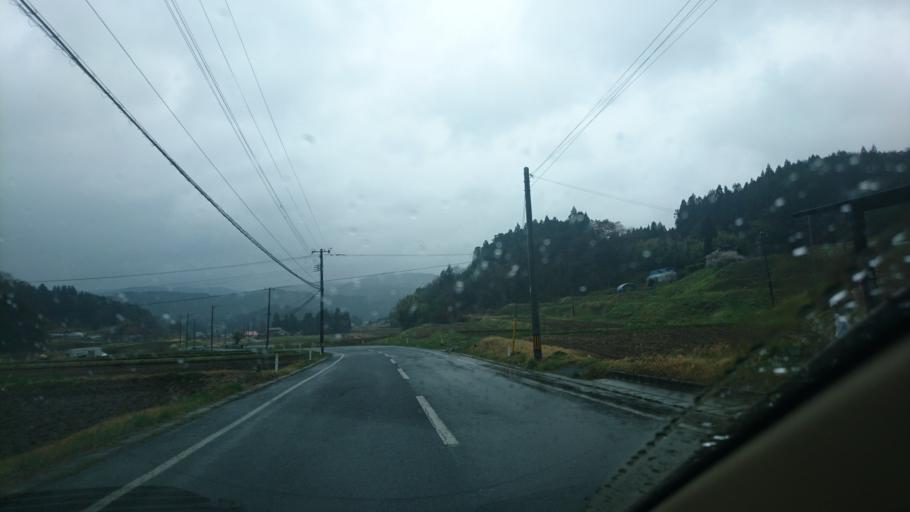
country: JP
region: Iwate
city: Ofunato
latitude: 38.9497
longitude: 141.4626
